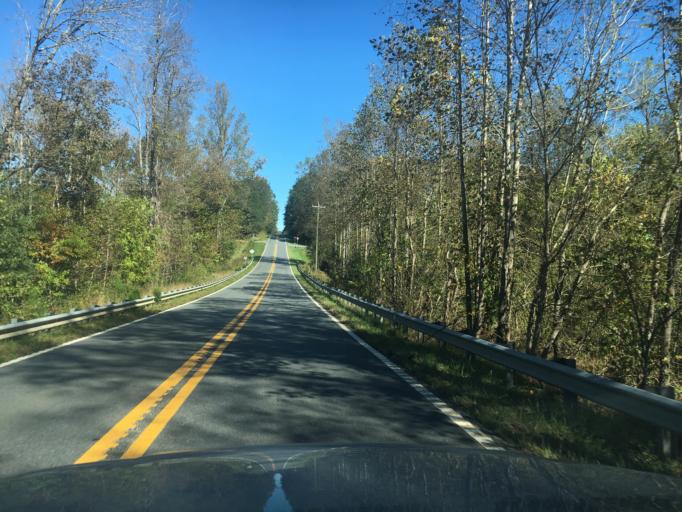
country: US
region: North Carolina
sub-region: Rutherford County
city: Spindale
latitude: 35.4604
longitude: -81.8858
